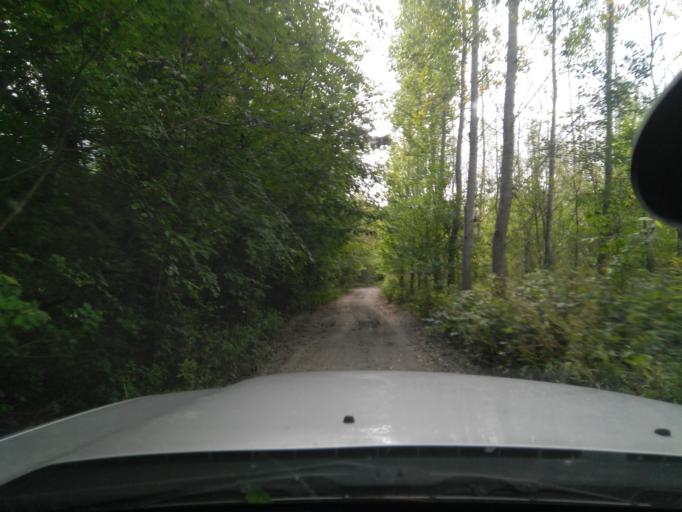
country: HU
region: Bacs-Kiskun
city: Apostag
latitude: 46.9034
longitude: 18.9519
